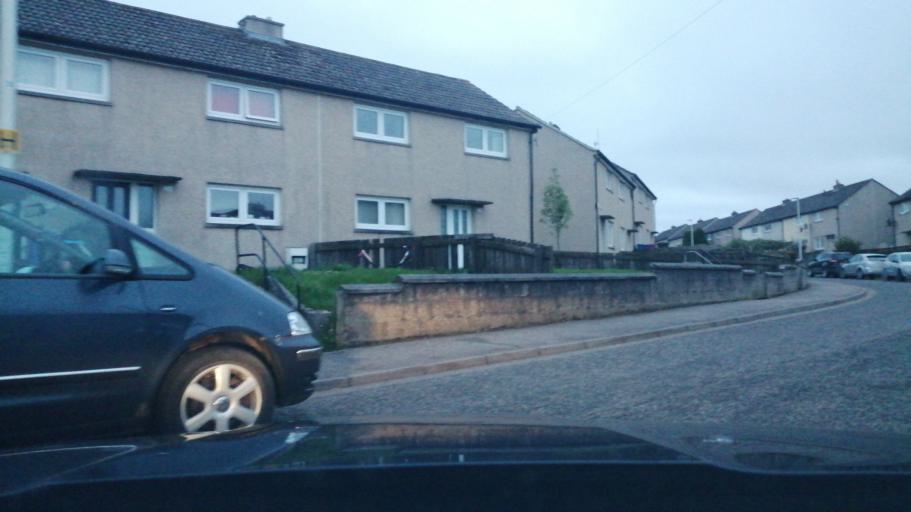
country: GB
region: Scotland
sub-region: Moray
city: Keith
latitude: 57.5405
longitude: -2.9560
